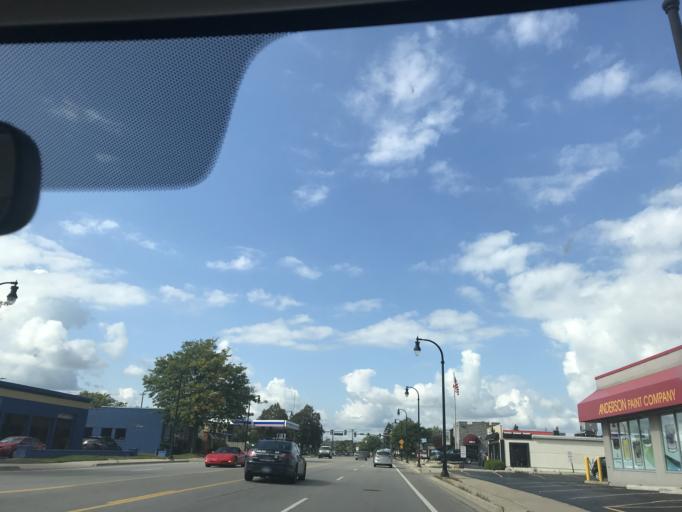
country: US
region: Michigan
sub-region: Washtenaw County
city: Ann Arbor
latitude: 42.2776
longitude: -83.7789
